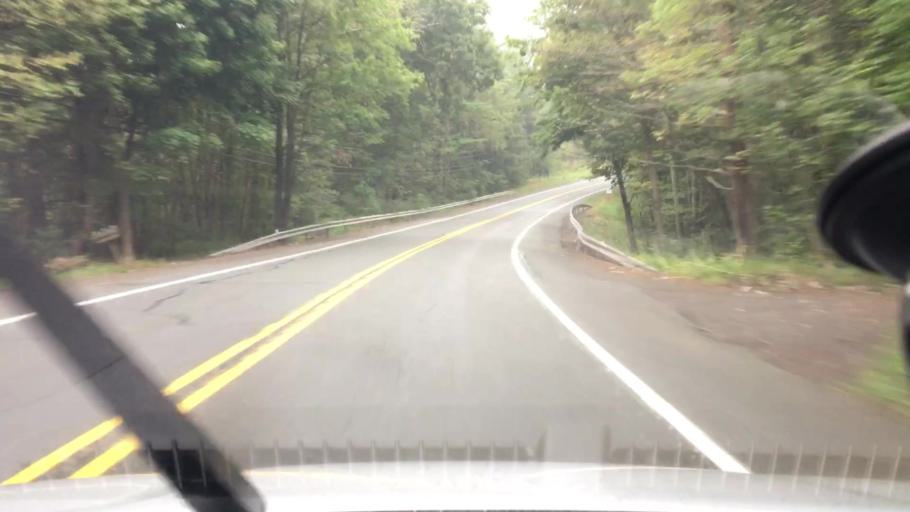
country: US
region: Pennsylvania
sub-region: Monroe County
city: Mountainhome
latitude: 41.1461
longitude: -75.2898
